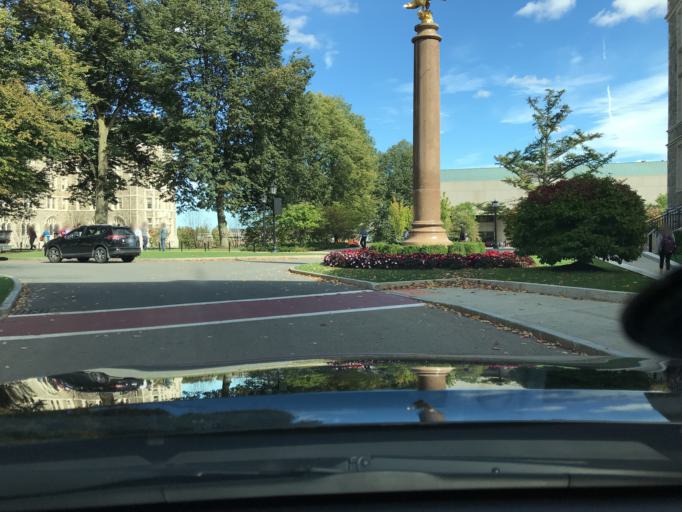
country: US
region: Massachusetts
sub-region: Middlesex County
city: Watertown
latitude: 42.3358
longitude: -71.1708
